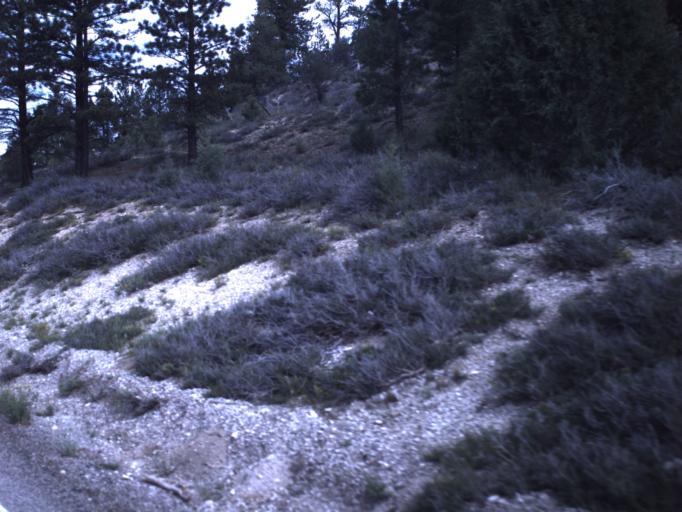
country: US
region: Utah
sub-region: Garfield County
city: Panguitch
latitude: 37.4913
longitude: -112.5708
